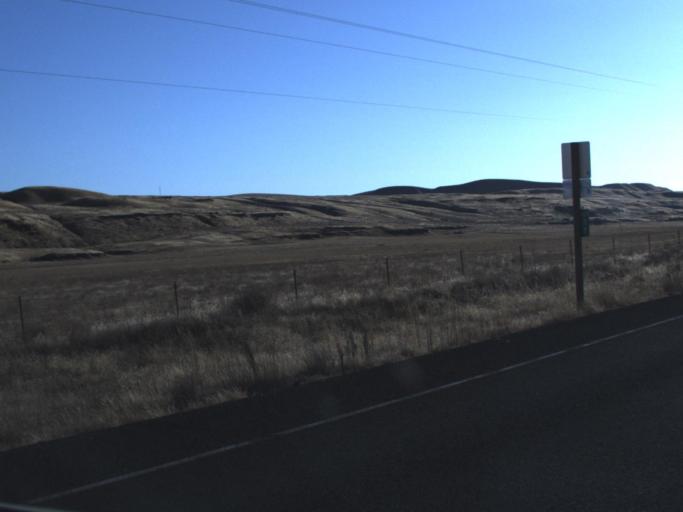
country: US
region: Washington
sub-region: Adams County
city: Ritzville
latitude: 46.7355
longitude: -118.3458
